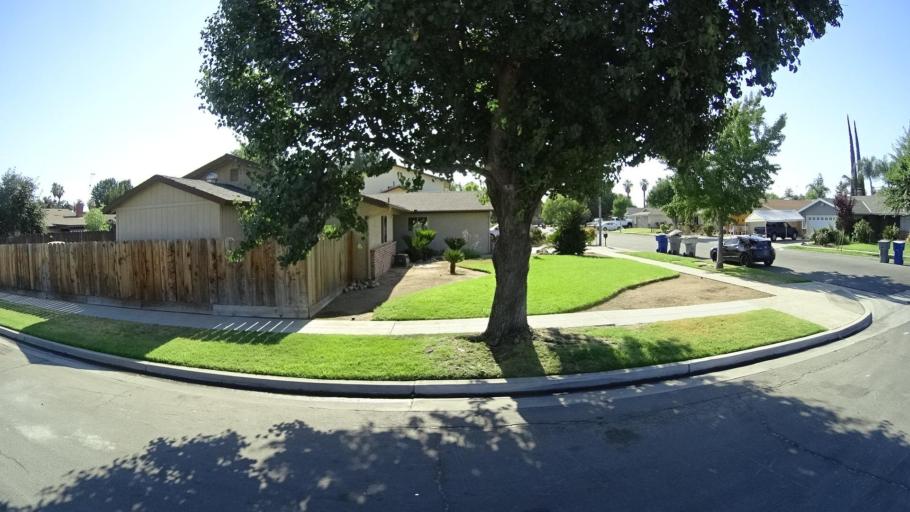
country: US
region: California
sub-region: Fresno County
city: Sunnyside
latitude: 36.7451
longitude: -119.7201
